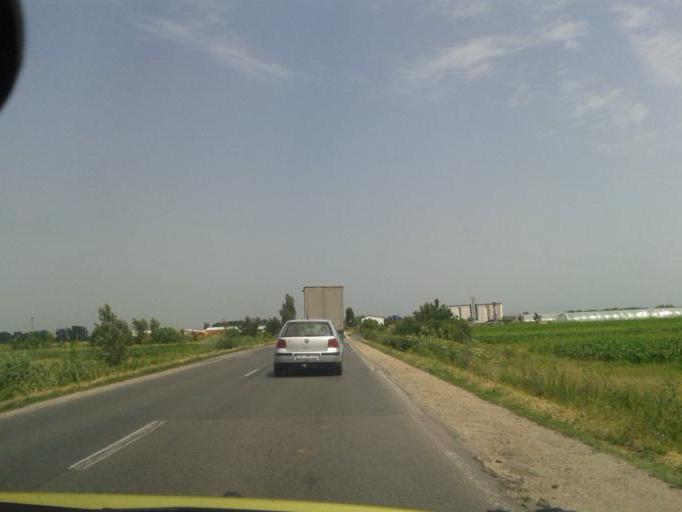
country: RO
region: Dambovita
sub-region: Oras Gaesti
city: Gaesti
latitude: 44.6976
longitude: 25.3116
